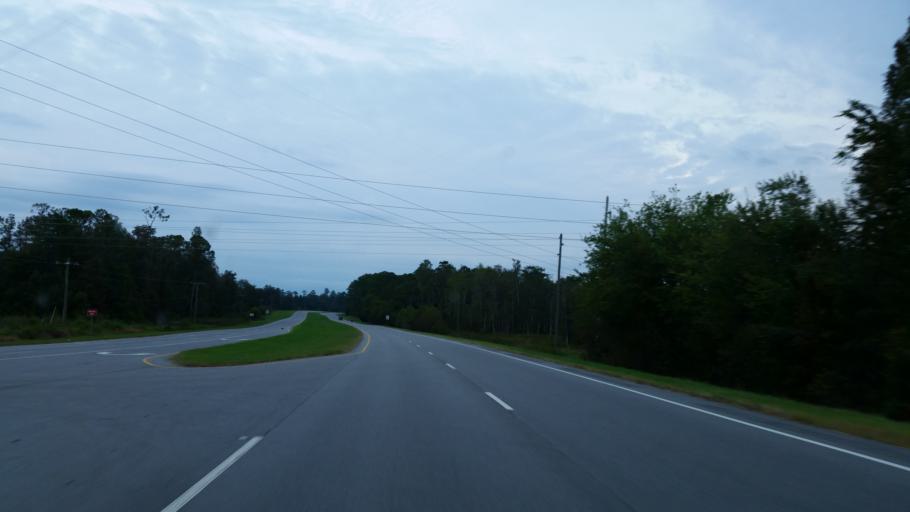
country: US
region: Georgia
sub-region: Lowndes County
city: Valdosta
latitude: 30.7280
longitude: -83.2196
